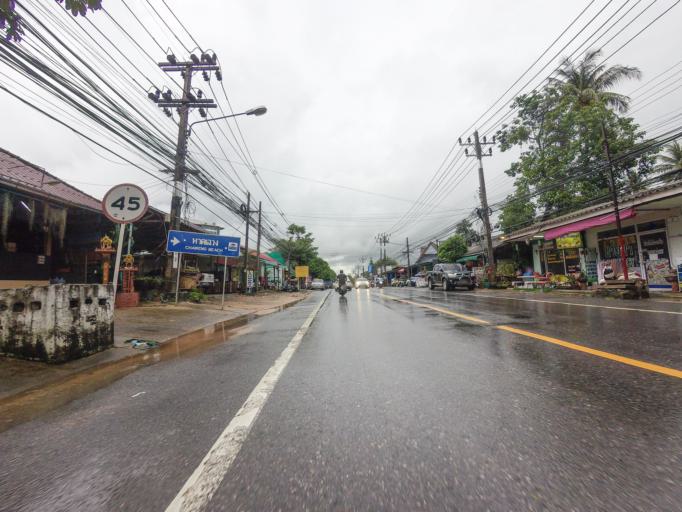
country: TH
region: Surat Thani
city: Ko Samui
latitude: 9.5099
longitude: 100.0524
